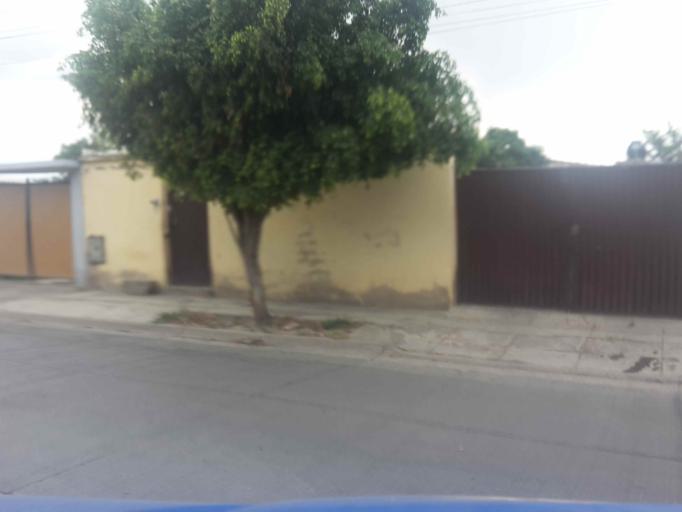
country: BO
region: Cochabamba
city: Cochabamba
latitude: -17.3767
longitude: -66.1904
